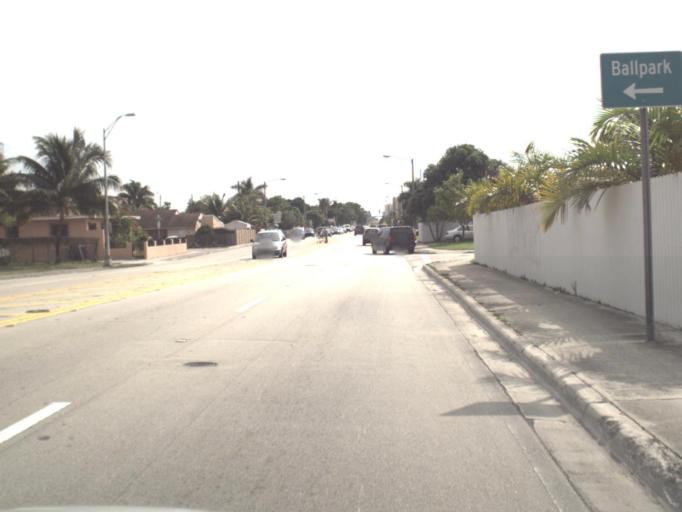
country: US
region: Florida
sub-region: Miami-Dade County
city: Brownsville
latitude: 25.7857
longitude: -80.2559
